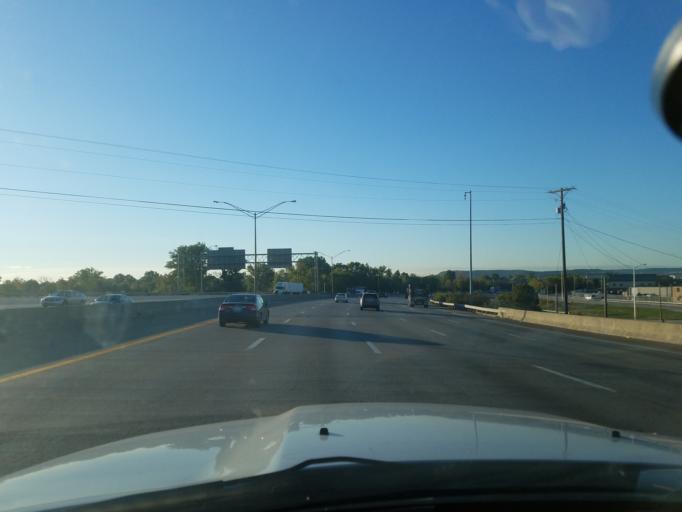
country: US
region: Kentucky
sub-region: Jefferson County
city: Audubon Park
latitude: 38.1787
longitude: -85.7199
